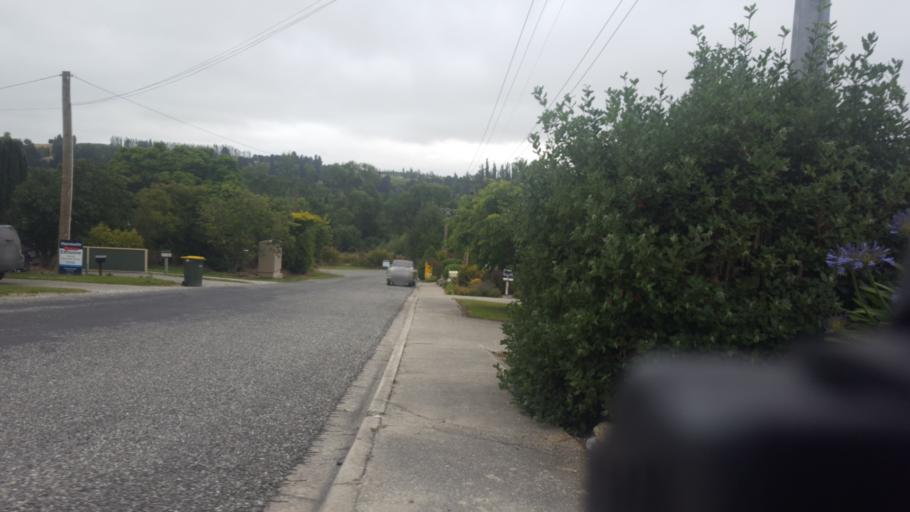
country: NZ
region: Otago
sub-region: Queenstown-Lakes District
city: Kingston
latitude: -45.5362
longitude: 169.3083
